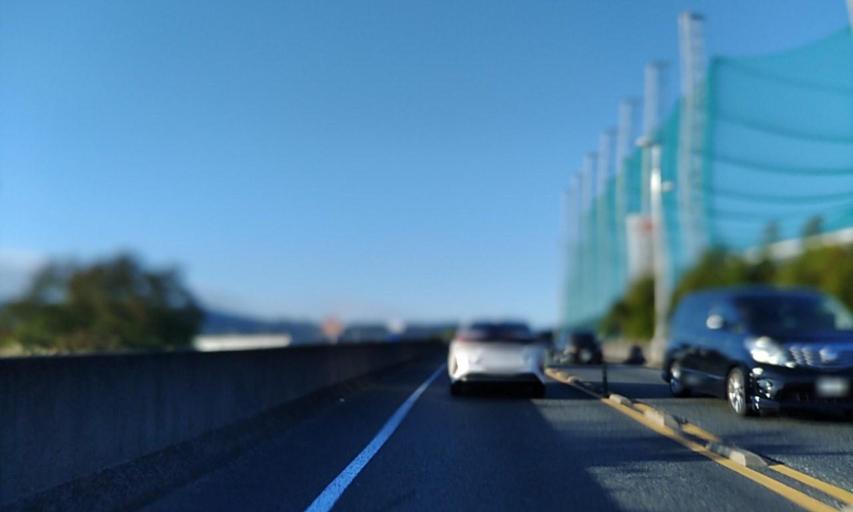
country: JP
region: Wakayama
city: Iwade
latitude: 34.3537
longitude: 135.2607
